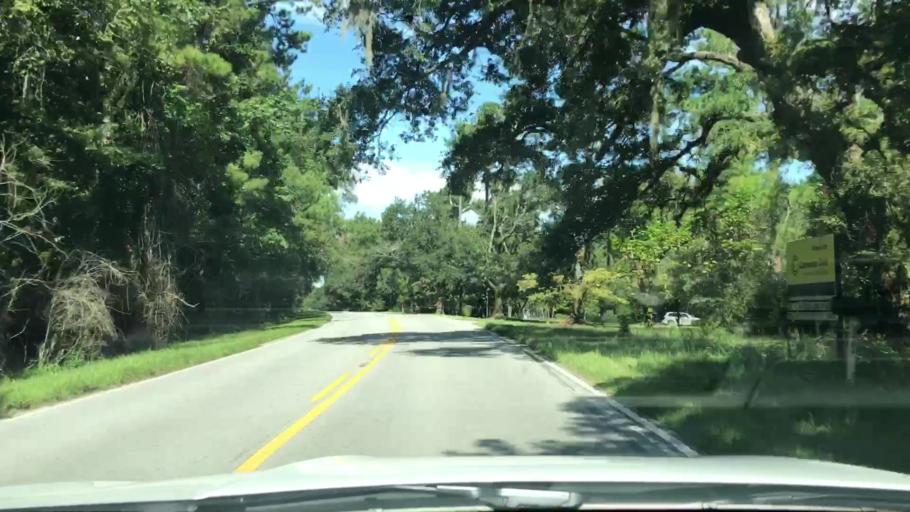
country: US
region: South Carolina
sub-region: Dorchester County
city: Centerville
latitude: 32.9452
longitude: -80.1955
